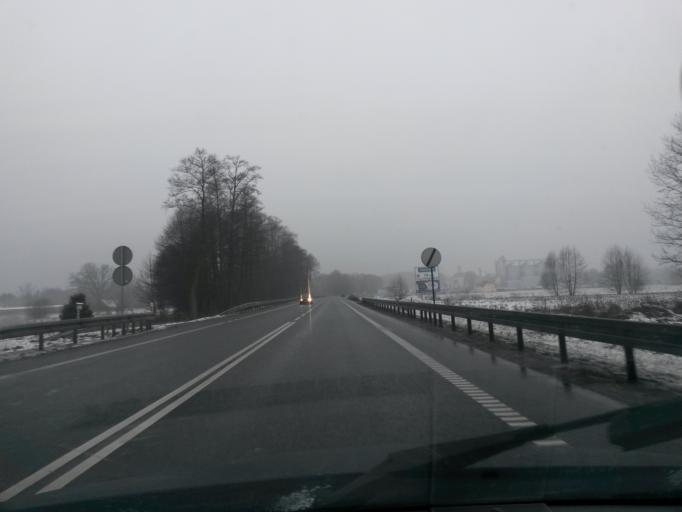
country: PL
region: Kujawsko-Pomorskie
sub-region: Powiat bydgoski
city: Solec Kujawski
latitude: 53.0641
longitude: 18.1709
